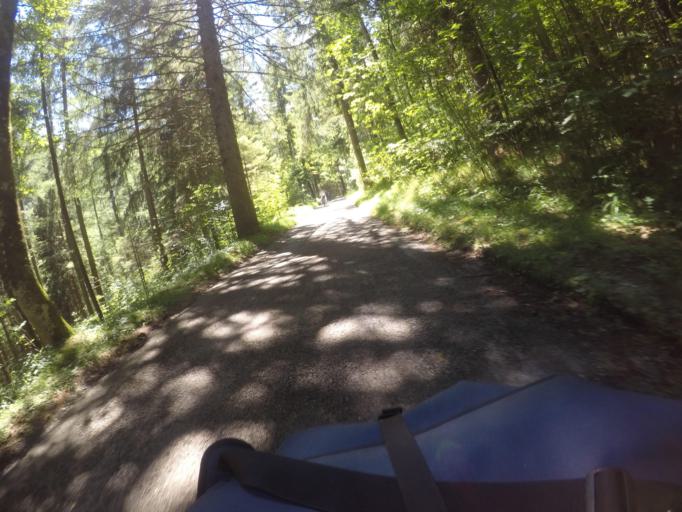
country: AT
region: Tyrol
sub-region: Politischer Bezirk Reutte
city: Musau
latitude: 47.5624
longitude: 10.6715
